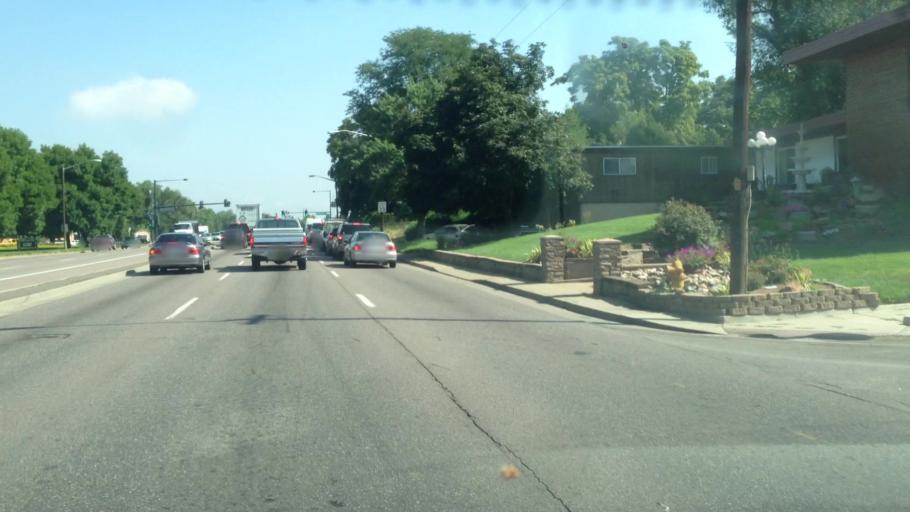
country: US
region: Colorado
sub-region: Adams County
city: Commerce City
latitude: 39.7601
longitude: -104.9405
